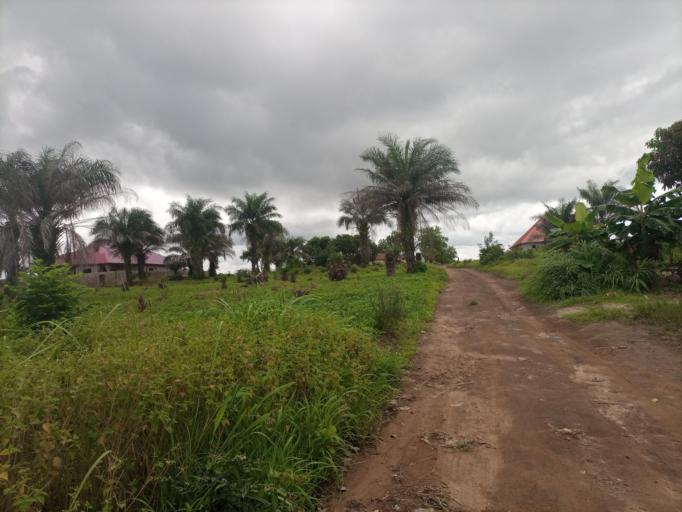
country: SL
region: Northern Province
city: Masoyila
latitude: 8.5686
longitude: -13.1568
